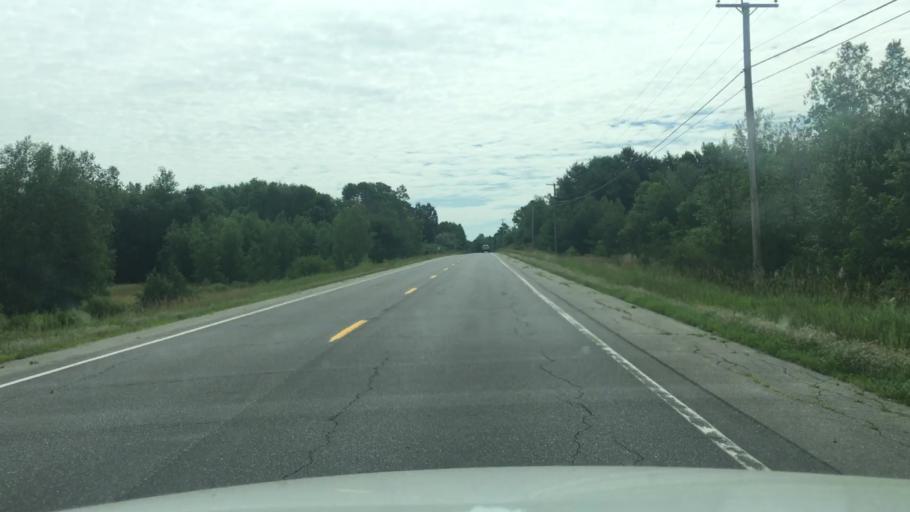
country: US
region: Maine
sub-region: Waldo County
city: Burnham
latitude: 44.6159
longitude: -69.3803
